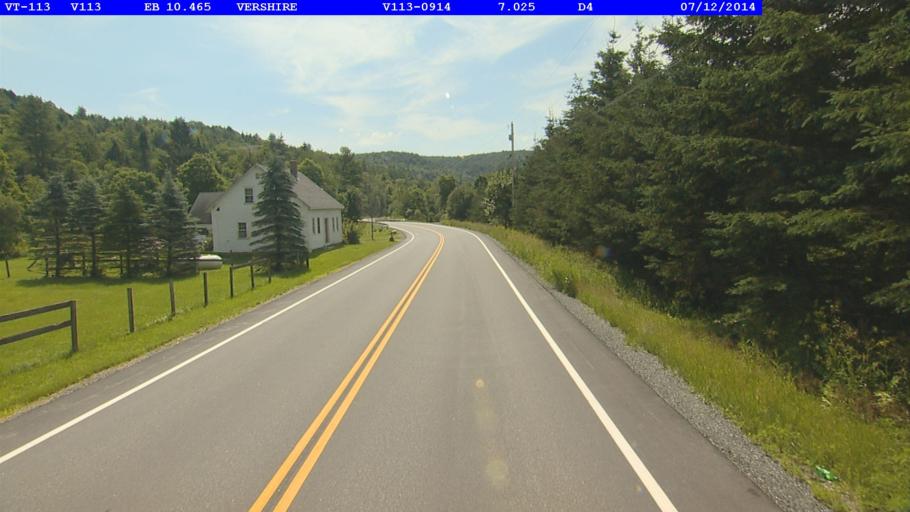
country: US
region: New Hampshire
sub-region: Grafton County
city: Orford
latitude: 43.9451
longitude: -72.2714
